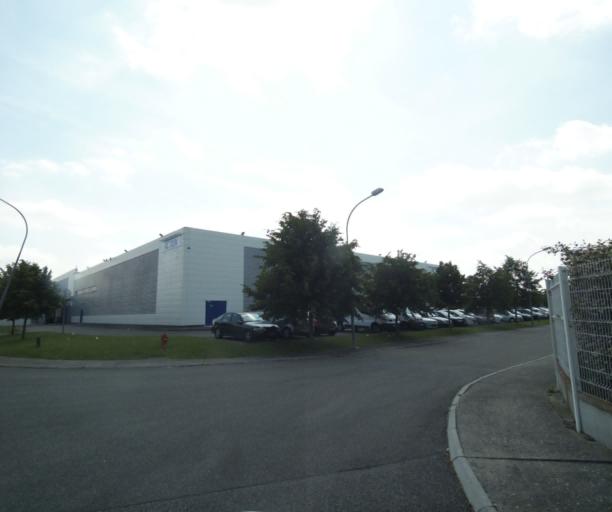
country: FR
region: Midi-Pyrenees
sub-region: Departement du Tarn-et-Garonne
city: Montauban
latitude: 44.0396
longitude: 1.3862
